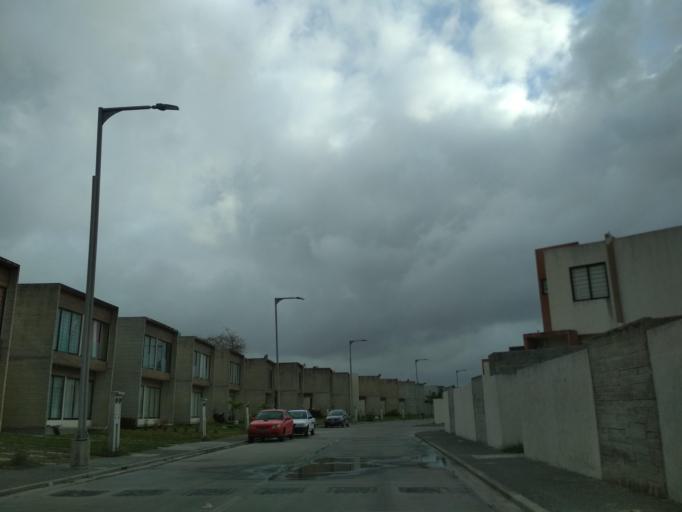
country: MX
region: Veracruz
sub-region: Veracruz
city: Fraccionamiento Geovillas los Pinos
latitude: 19.2204
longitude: -96.2297
